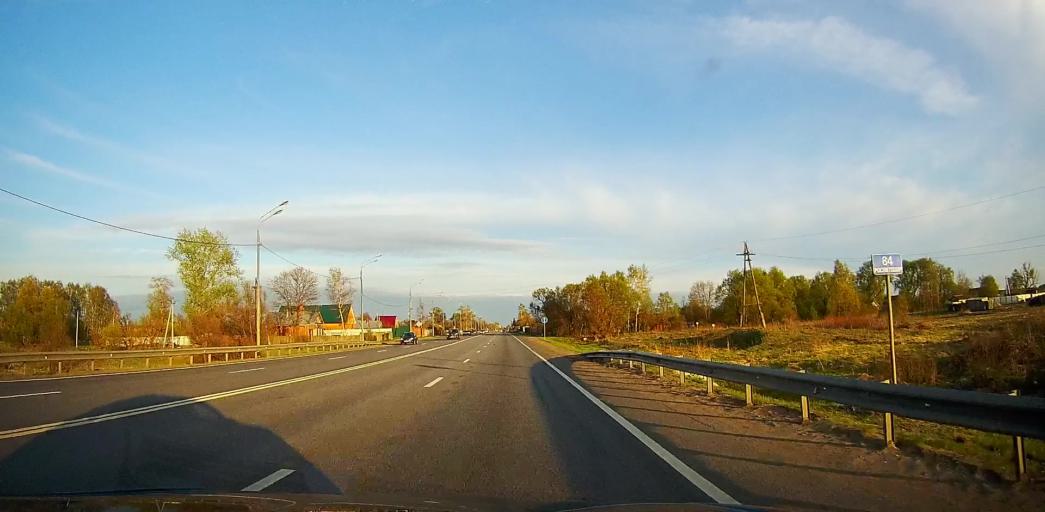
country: RU
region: Moskovskaya
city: Troitskoye
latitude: 55.2547
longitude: 38.5182
